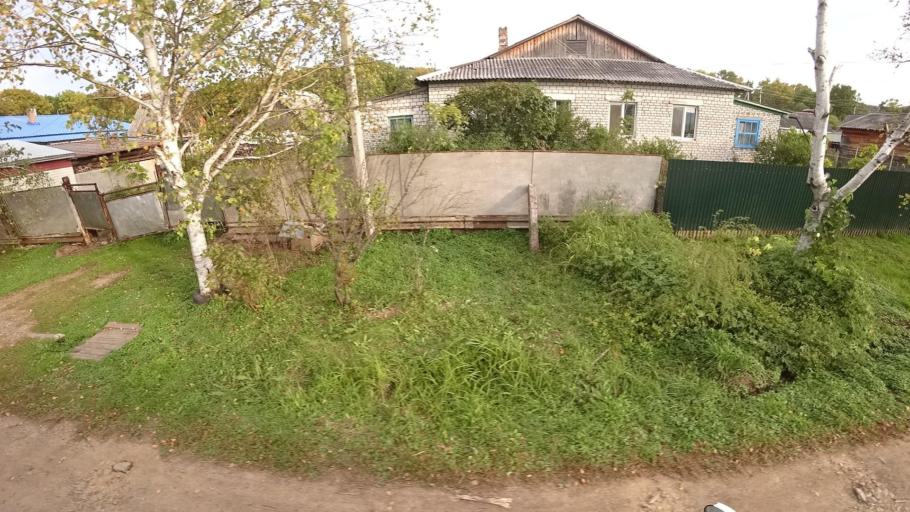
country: RU
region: Primorskiy
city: Yakovlevka
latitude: 44.4178
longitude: 133.4552
